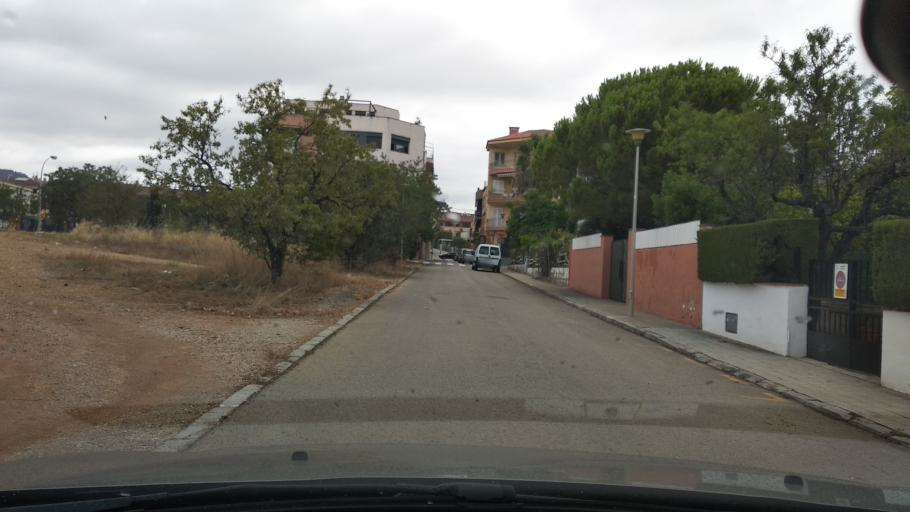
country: ES
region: Catalonia
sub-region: Provincia de Tarragona
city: El Vendrell
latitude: 41.2150
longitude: 1.5273
